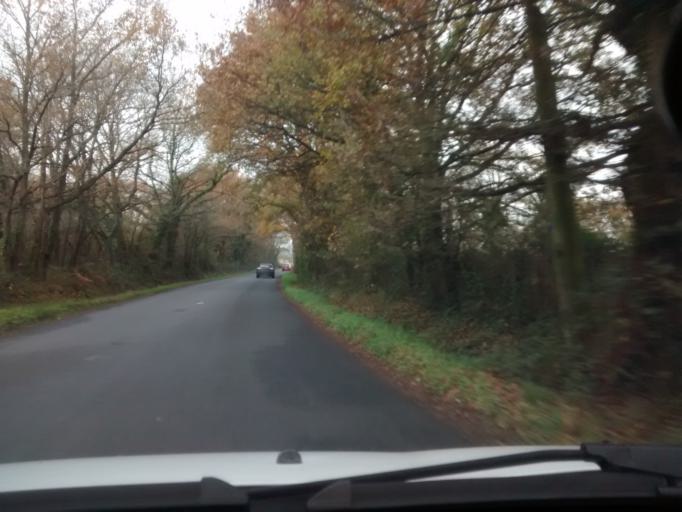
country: FR
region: Brittany
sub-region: Departement d'Ille-et-Vilaine
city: Saint-Jacques-de-la-Lande
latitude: 48.0861
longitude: -1.7336
